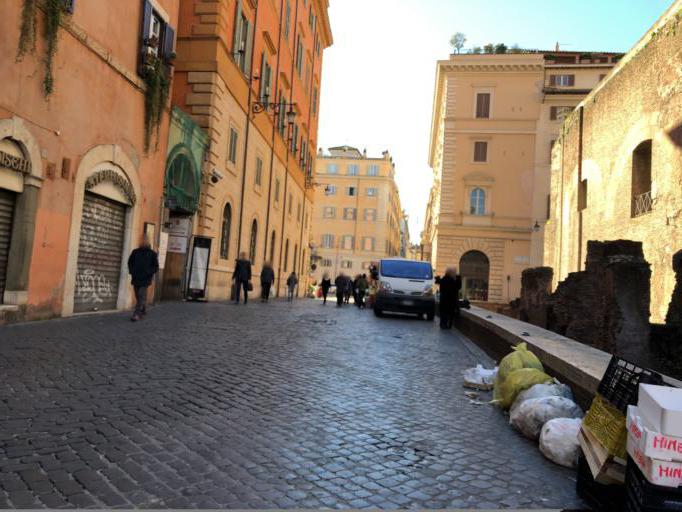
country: VA
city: Vatican City
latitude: 41.8987
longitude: 12.4773
